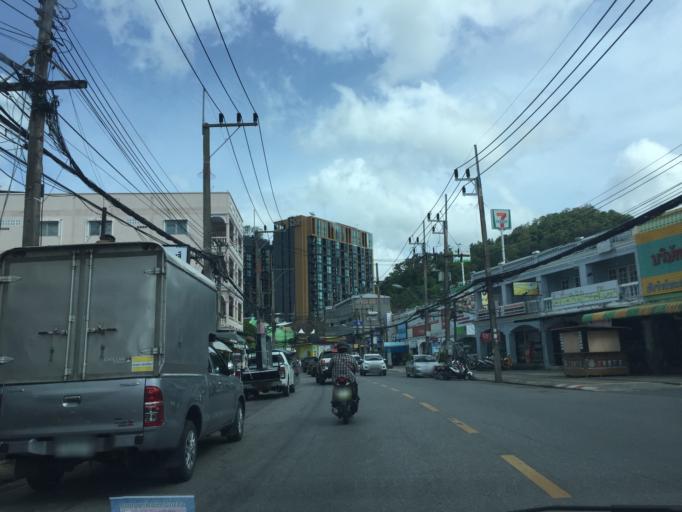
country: TH
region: Phuket
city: Wichit
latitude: 7.9034
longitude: 98.3777
